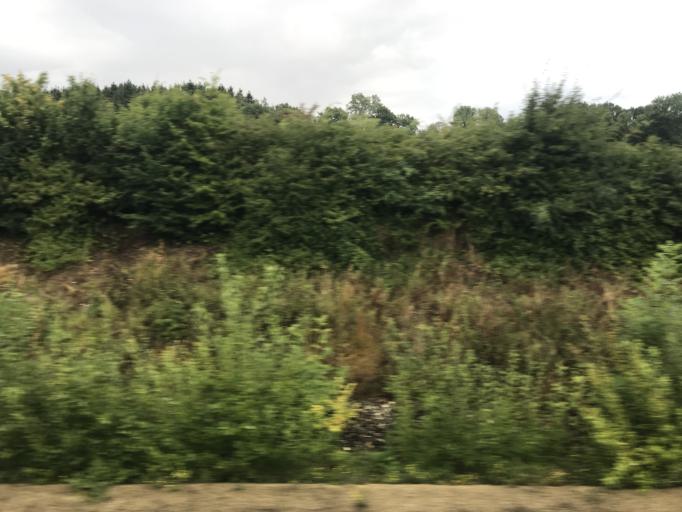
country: LU
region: Luxembourg
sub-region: Canton d'Esch-sur-Alzette
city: Reckange-sur-Mess
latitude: 49.5780
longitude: 6.0064
